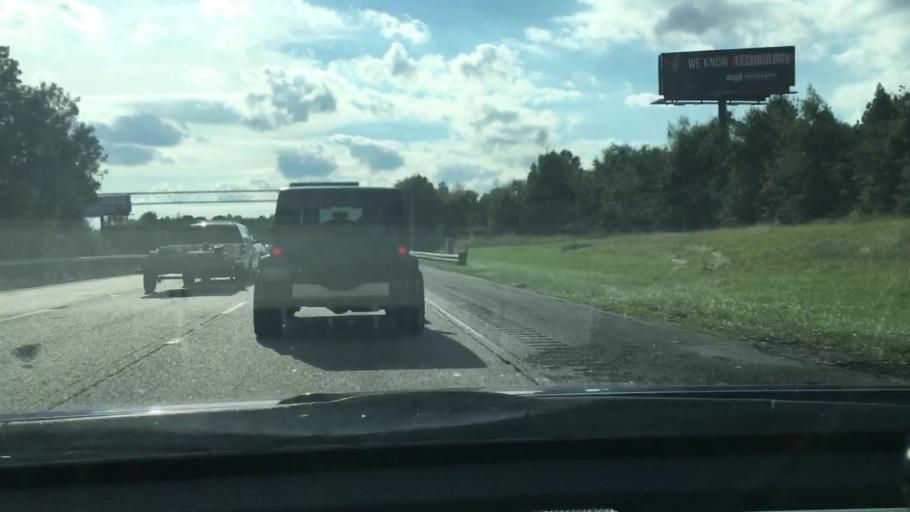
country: US
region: South Carolina
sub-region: Lexington County
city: West Columbia
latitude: 34.0516
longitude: -81.0650
